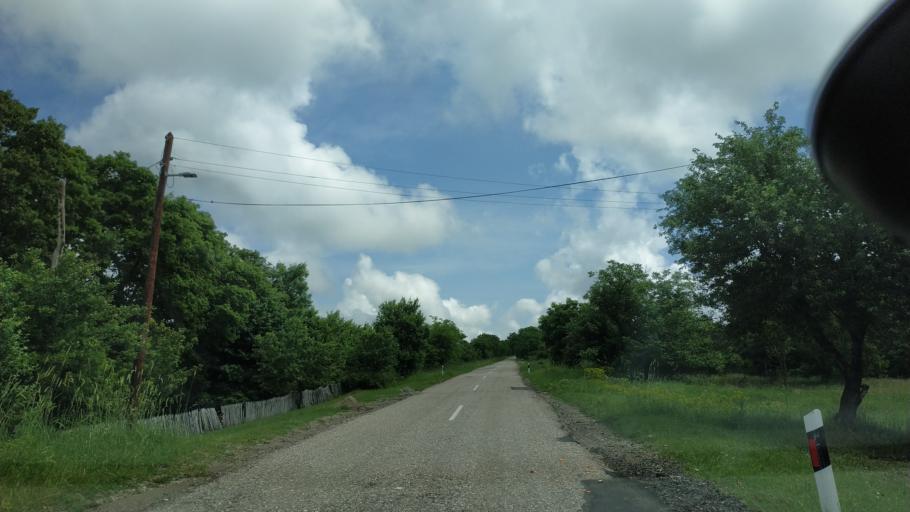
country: RS
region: Central Serbia
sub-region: Zajecarski Okrug
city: Boljevac
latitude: 43.8309
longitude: 21.9707
